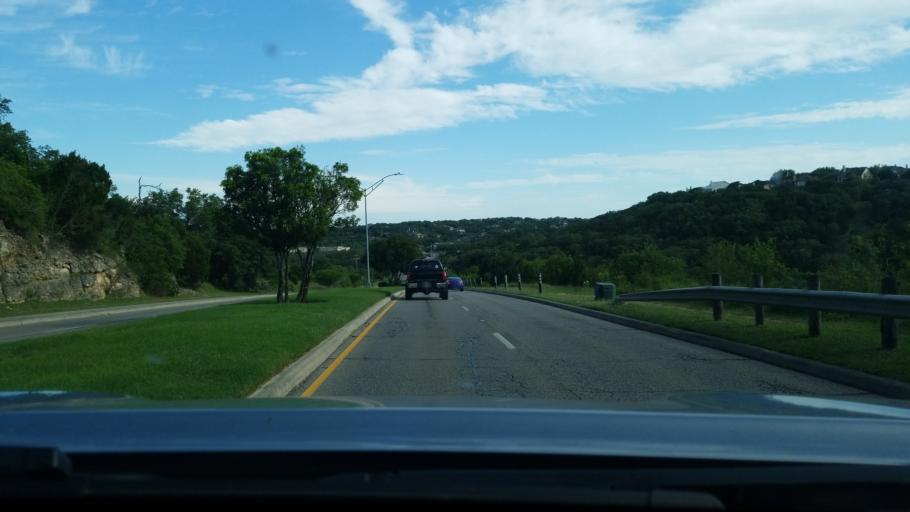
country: US
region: Texas
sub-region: Bexar County
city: Hollywood Park
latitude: 29.6496
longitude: -98.4812
